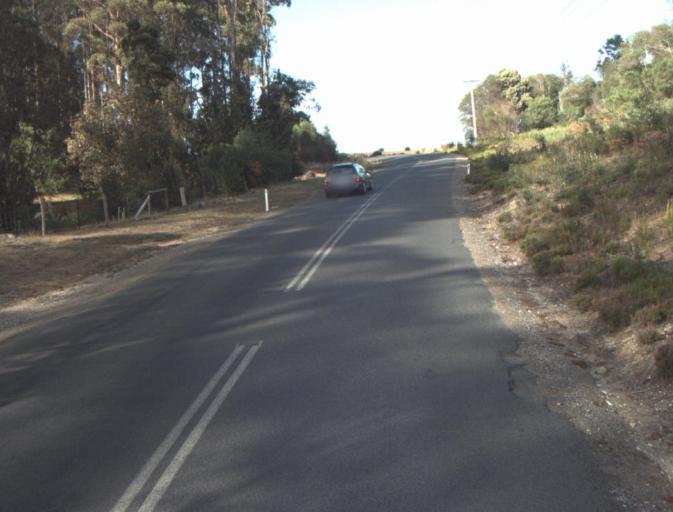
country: AU
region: Tasmania
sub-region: Launceston
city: Mayfield
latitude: -41.2038
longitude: 147.2166
